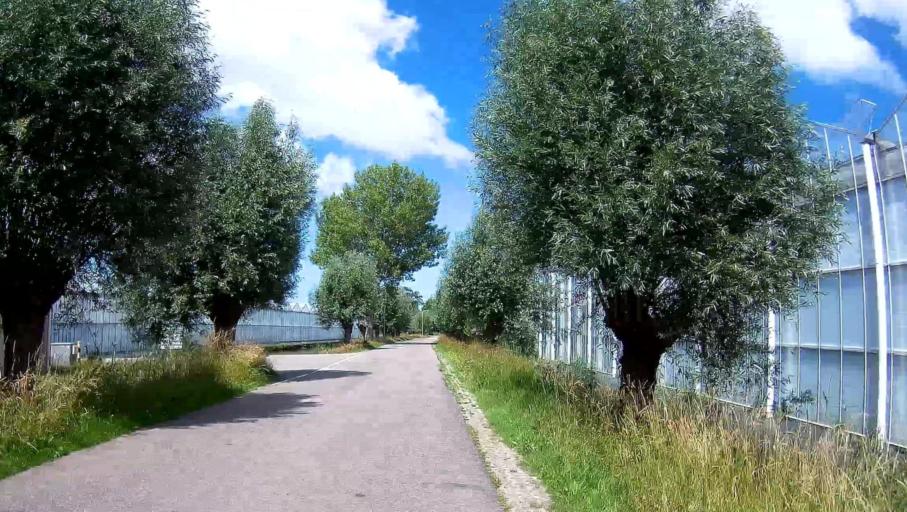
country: NL
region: South Holland
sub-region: Gemeente Westland
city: De Lier
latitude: 51.9885
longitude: 4.2606
